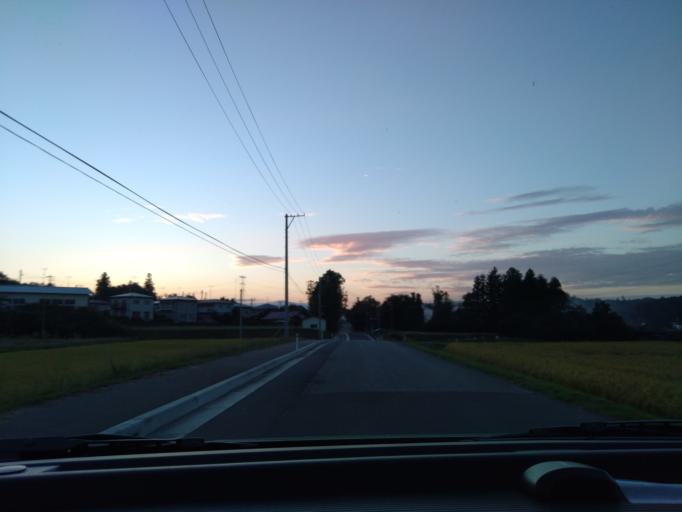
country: JP
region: Iwate
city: Ichinoseki
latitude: 38.8553
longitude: 141.1496
